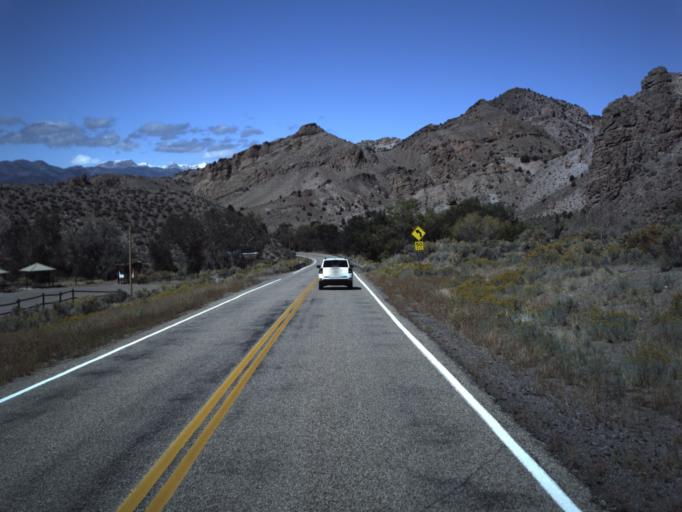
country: US
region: Utah
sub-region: Piute County
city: Junction
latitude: 38.1995
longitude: -112.1523
